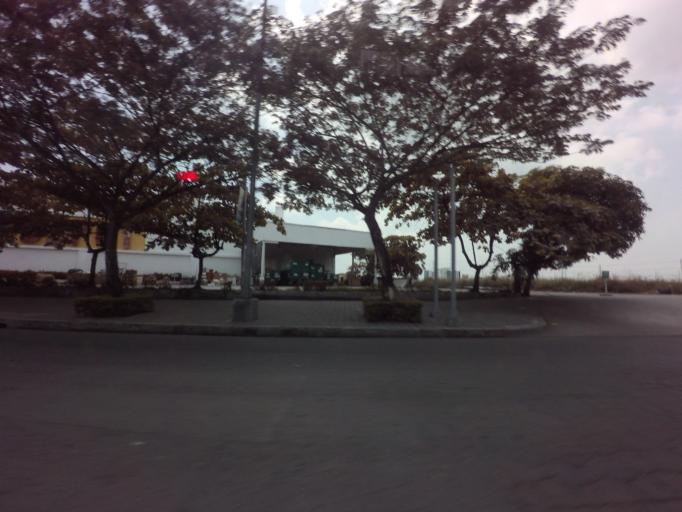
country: PH
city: Sambayanihan People's Village
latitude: 14.4213
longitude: 121.0412
